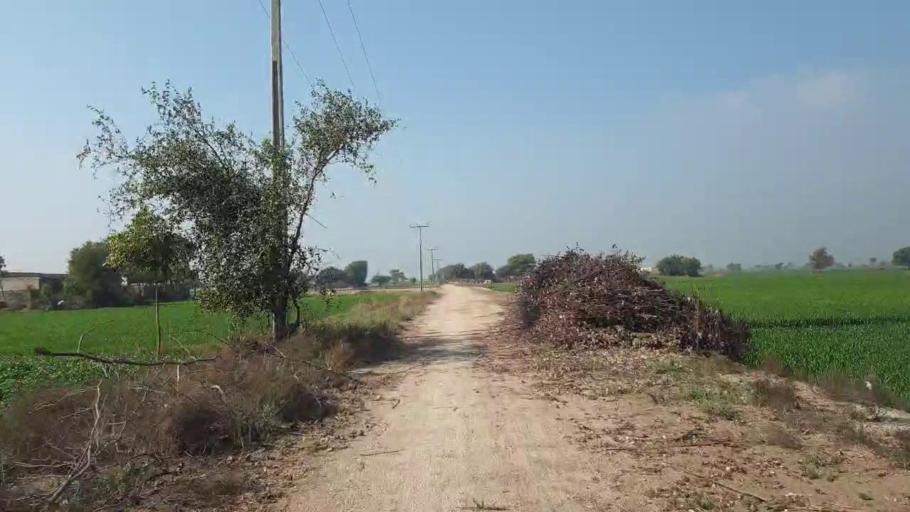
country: PK
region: Sindh
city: Shahdadpur
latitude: 26.0208
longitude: 68.5717
